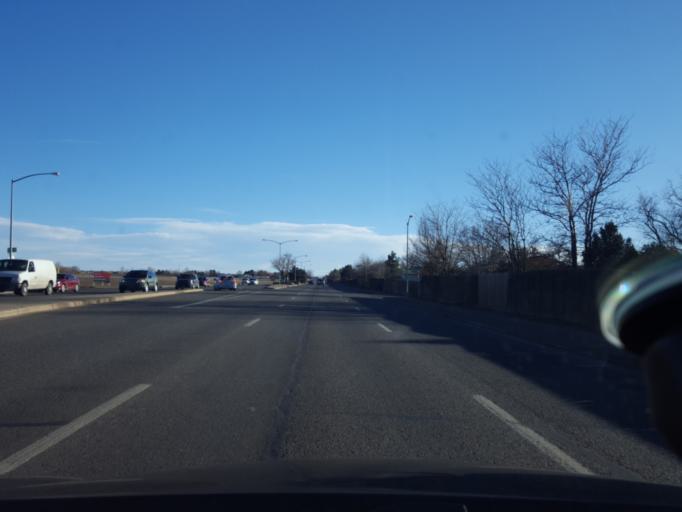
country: US
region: Colorado
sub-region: Adams County
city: Aurora
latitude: 39.7337
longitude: -104.7913
